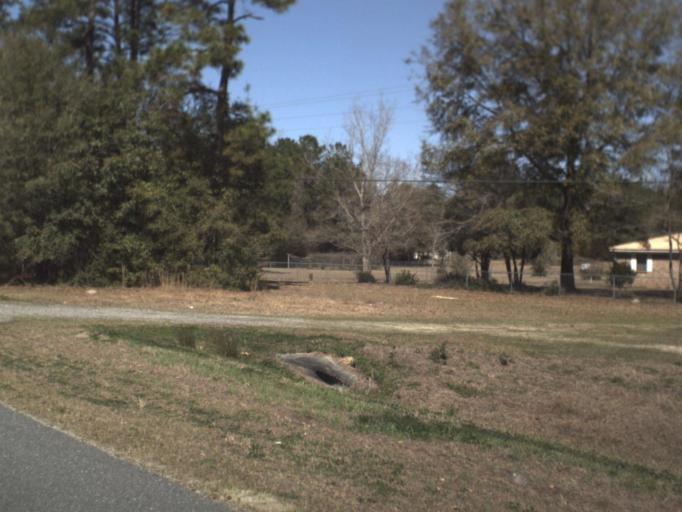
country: US
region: Florida
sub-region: Jackson County
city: Marianna
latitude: 30.7333
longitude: -85.0961
